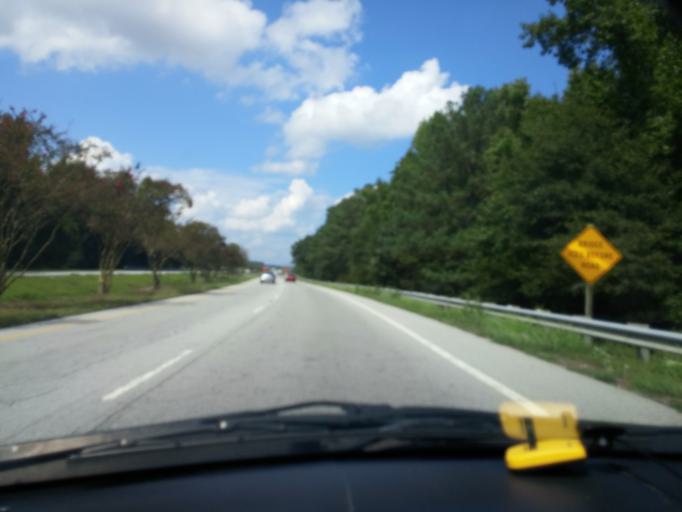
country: US
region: North Carolina
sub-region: Pitt County
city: Greenville
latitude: 35.6115
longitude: -77.3281
